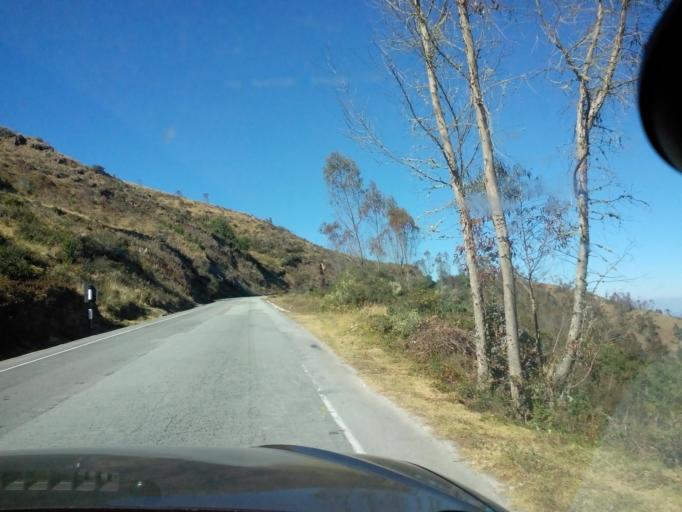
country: PE
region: Apurimac
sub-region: Provincia de Abancay
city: Tamburco
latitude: -13.5763
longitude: -72.8372
